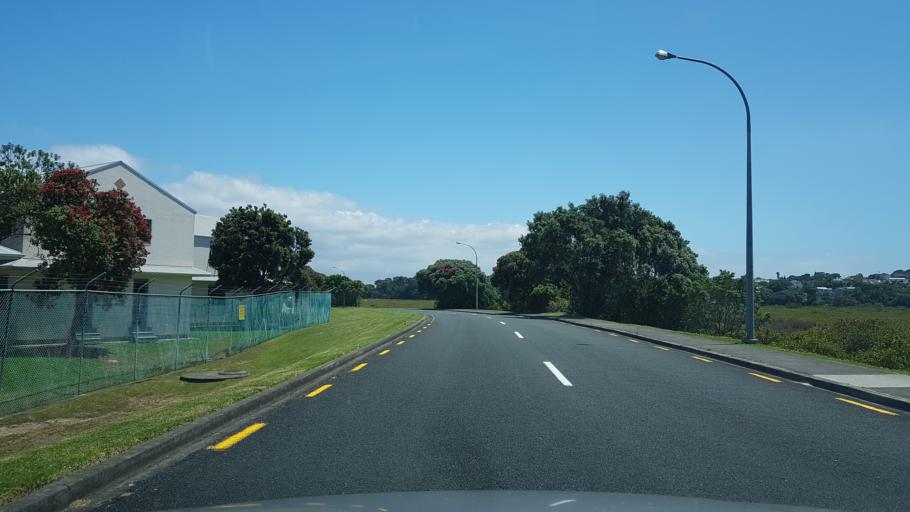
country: NZ
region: Auckland
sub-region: Auckland
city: North Shore
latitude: -36.8242
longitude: 174.7907
